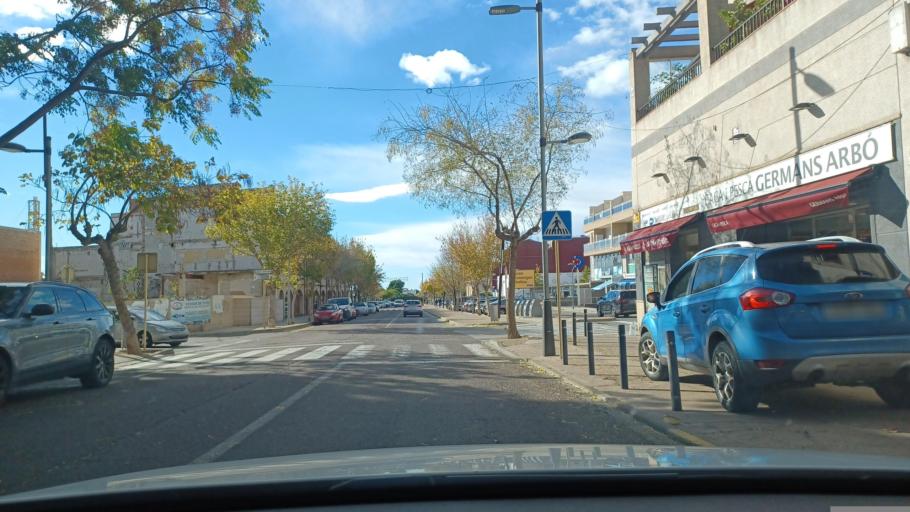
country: ES
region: Catalonia
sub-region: Provincia de Tarragona
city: Sant Carles de la Rapita
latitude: 40.6137
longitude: 0.5865
